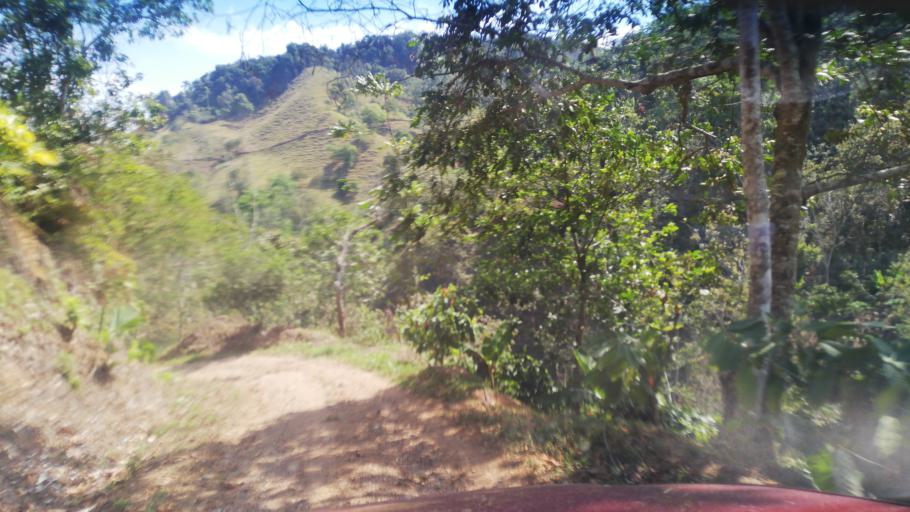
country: CO
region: Risaralda
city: Balboa
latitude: 4.9089
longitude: -75.9521
